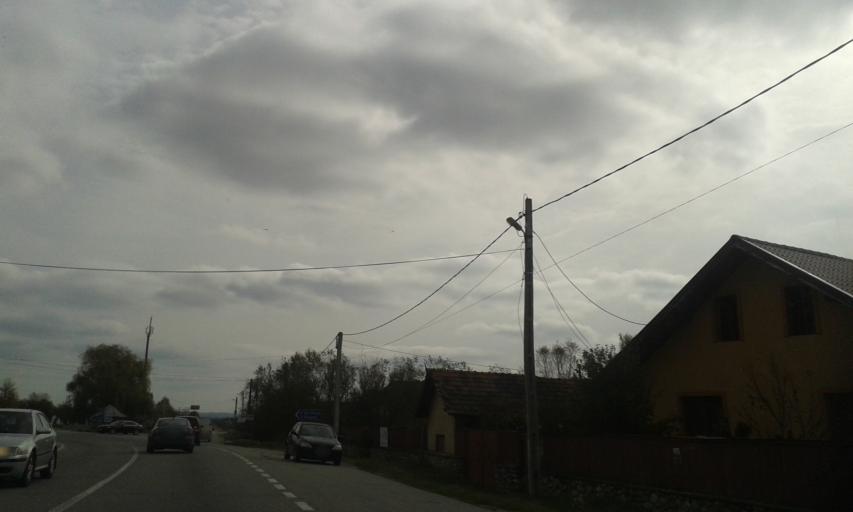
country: RO
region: Gorj
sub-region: Comuna Scoarta
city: Scoarta
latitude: 45.0173
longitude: 23.4664
